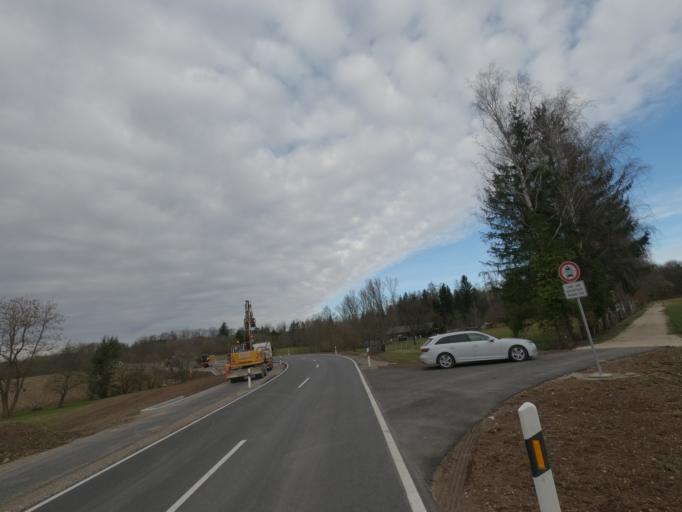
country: DE
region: Baden-Wuerttemberg
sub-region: Regierungsbezirk Stuttgart
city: Ohmden
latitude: 48.6543
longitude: 9.5334
